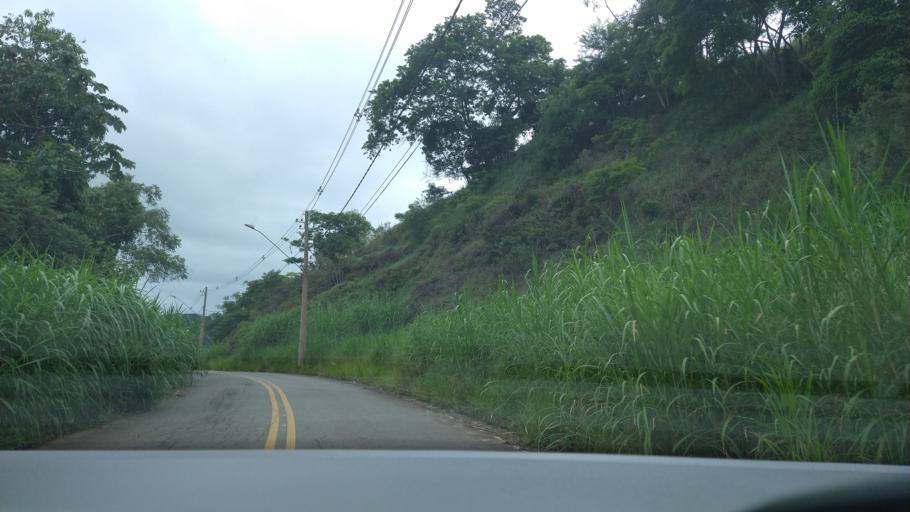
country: BR
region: Minas Gerais
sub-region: Vicosa
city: Vicosa
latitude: -20.7751
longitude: -42.8618
